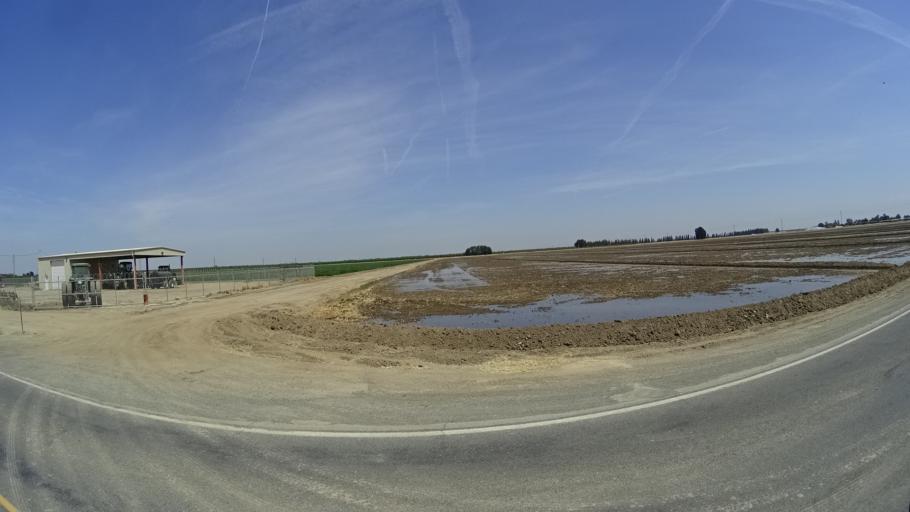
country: US
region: California
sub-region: Kings County
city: Lucerne
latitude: 36.4013
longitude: -119.5875
